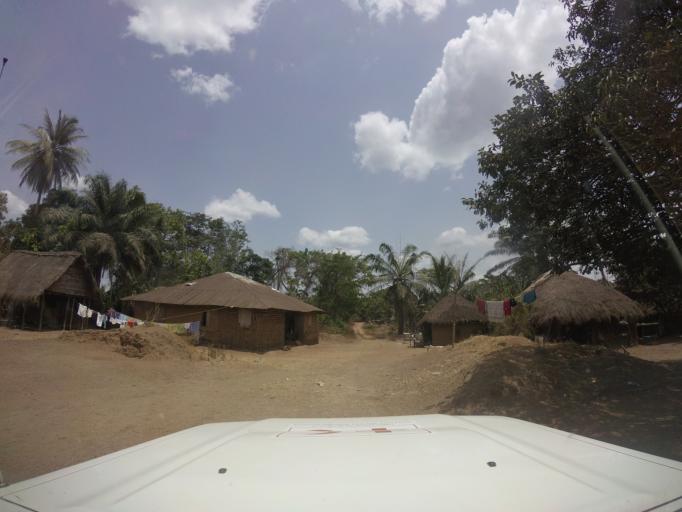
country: LR
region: Grand Cape Mount
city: Robertsport
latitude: 6.9864
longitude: -11.4029
